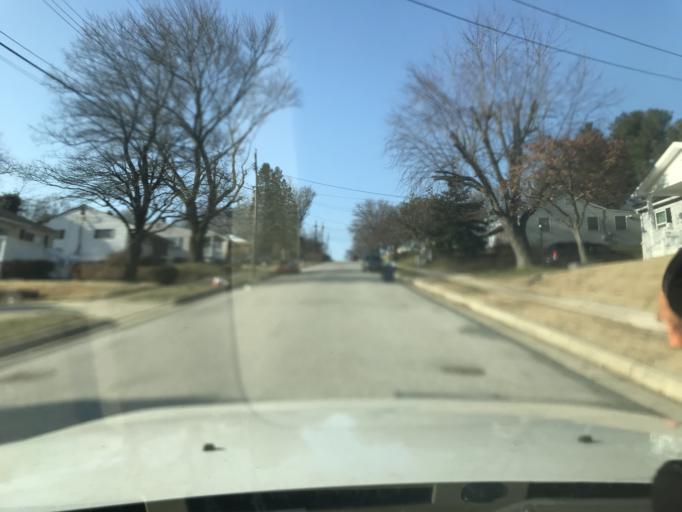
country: US
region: Maryland
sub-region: Baltimore County
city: Owings Mills
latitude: 39.4192
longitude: -76.7910
